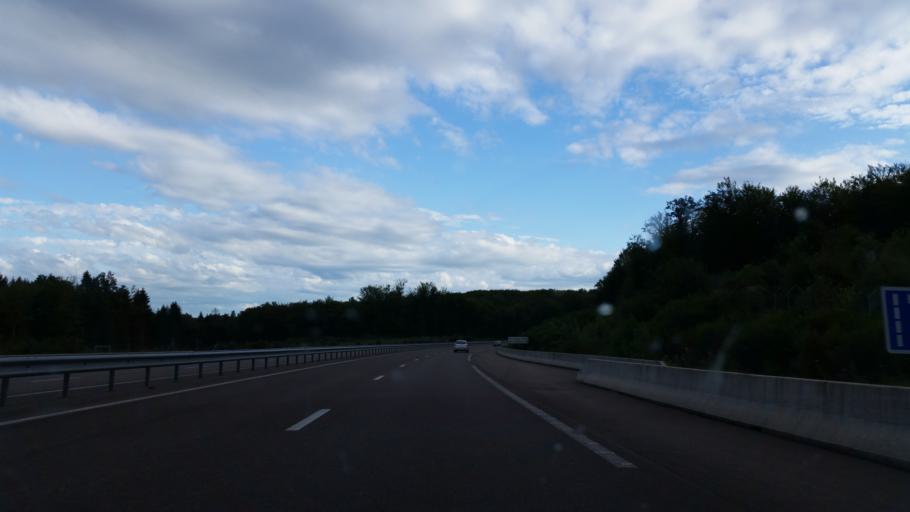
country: FR
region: Franche-Comte
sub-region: Departement de la Haute-Saone
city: Froideconche
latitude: 47.8361
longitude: 6.4031
